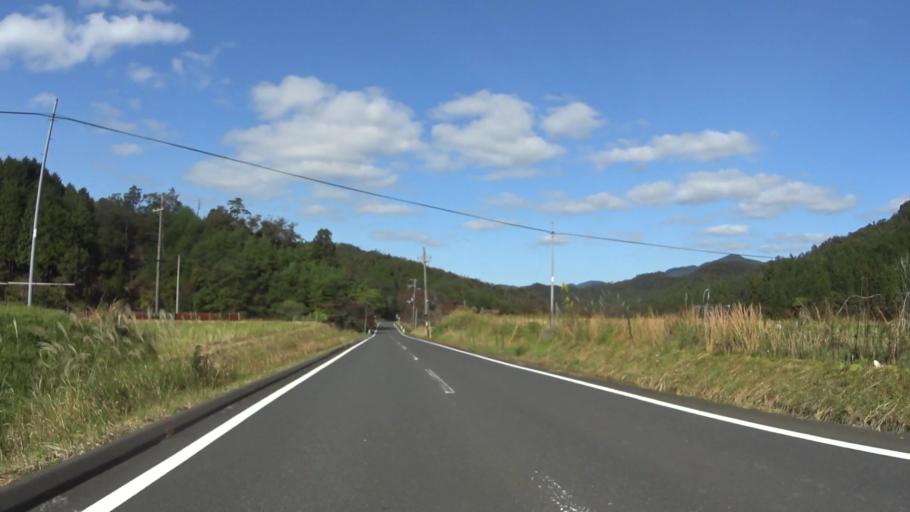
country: JP
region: Hyogo
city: Toyooka
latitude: 35.5505
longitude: 134.9774
